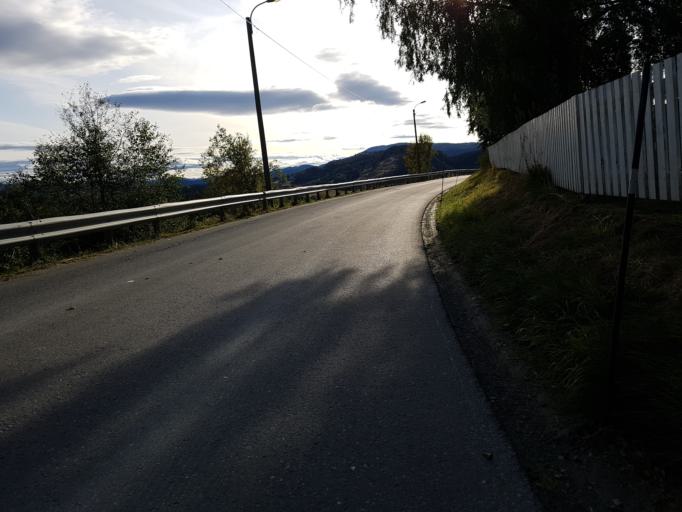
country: NO
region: Sor-Trondelag
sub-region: Klaebu
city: Klaebu
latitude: 63.3474
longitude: 10.4823
